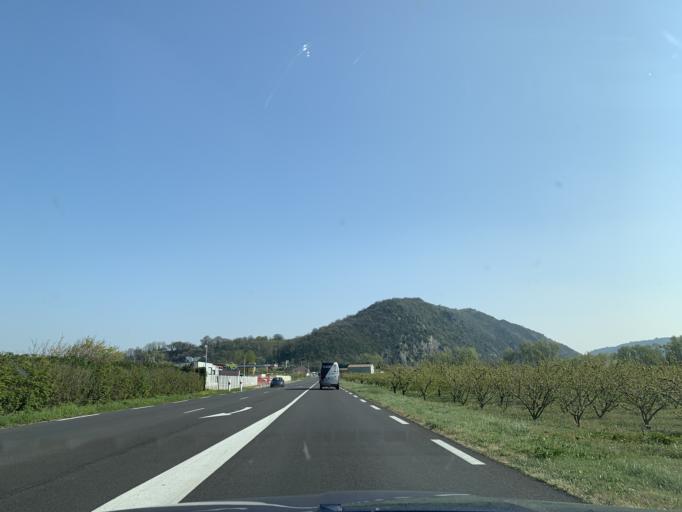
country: FR
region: Rhone-Alpes
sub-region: Departement de l'Ardeche
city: Saint-Jean-de-Muzols
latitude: 45.0992
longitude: 4.8331
